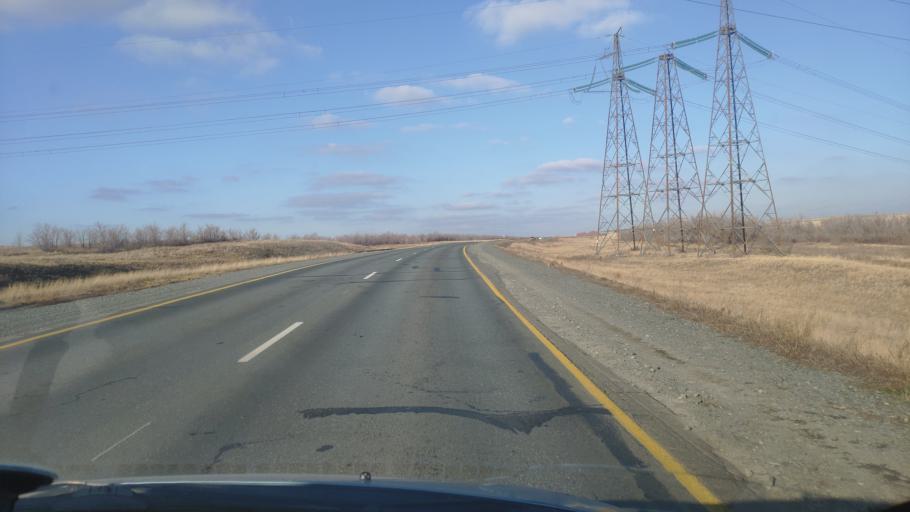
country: RU
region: Orenburg
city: Gay
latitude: 51.3628
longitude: 58.3907
